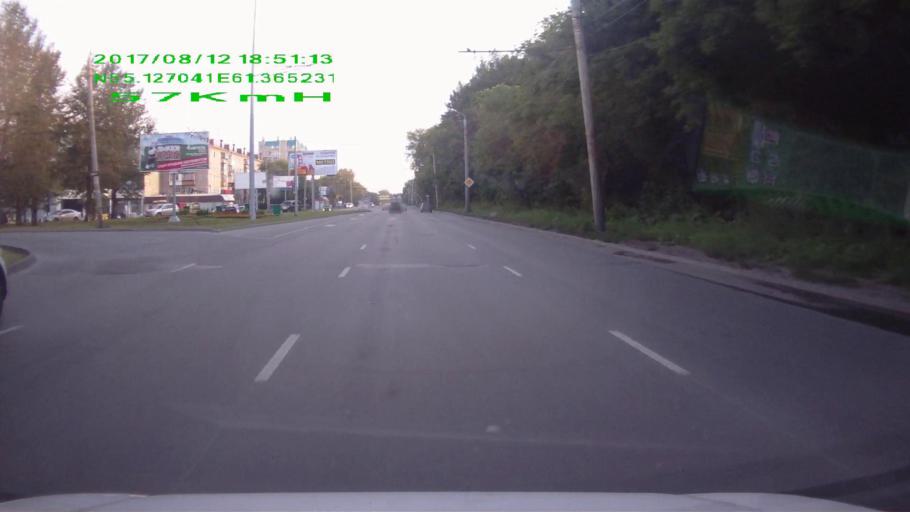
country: RU
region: Chelyabinsk
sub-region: Gorod Chelyabinsk
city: Chelyabinsk
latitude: 55.1240
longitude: 61.3640
